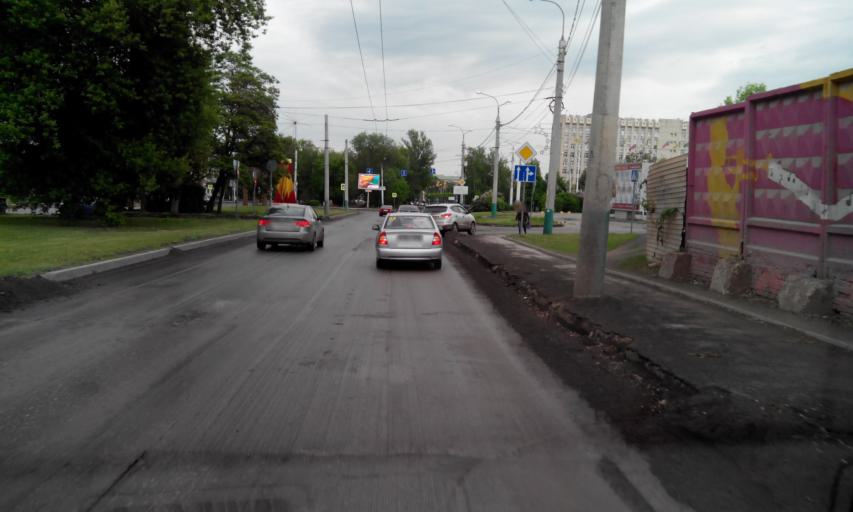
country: RU
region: Penza
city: Penza
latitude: 53.1960
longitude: 45.0080
